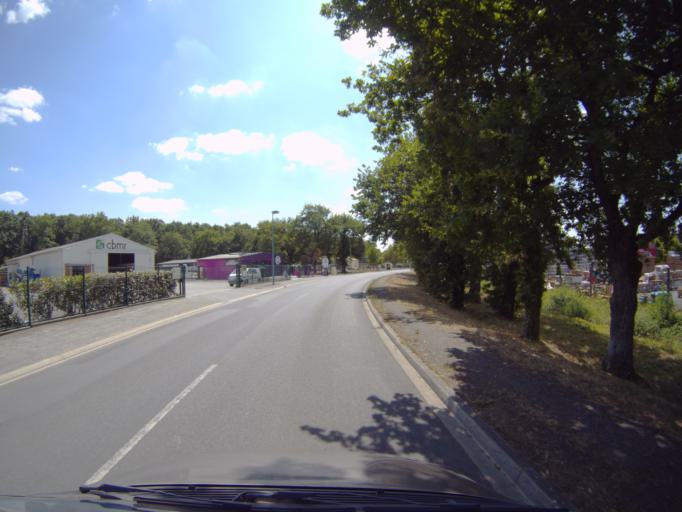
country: FR
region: Pays de la Loire
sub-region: Departement de la Loire-Atlantique
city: Aigrefeuille-sur-Maine
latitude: 47.0793
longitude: -1.4126
